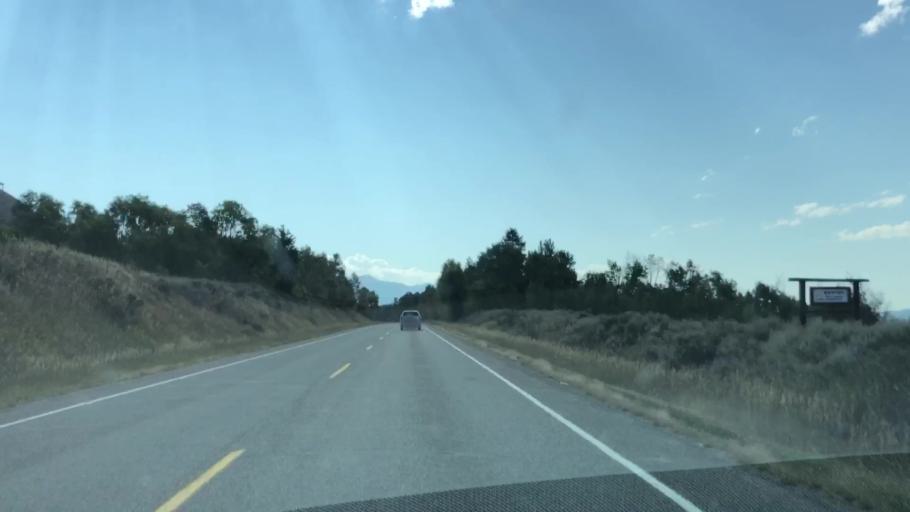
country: US
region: Wyoming
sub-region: Teton County
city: Hoback
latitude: 43.2122
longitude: -111.0603
